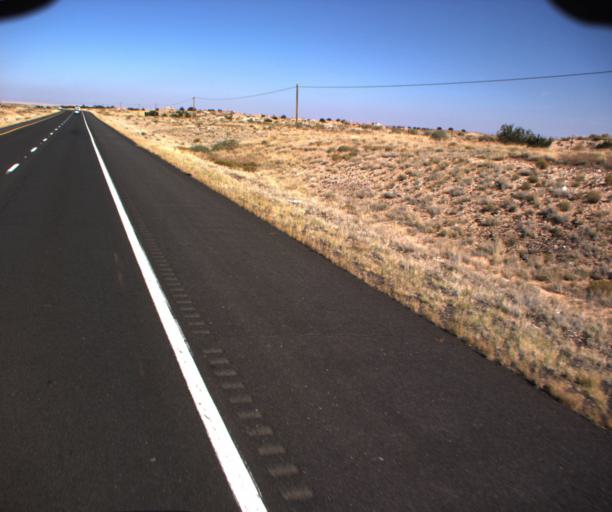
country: US
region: Arizona
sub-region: Coconino County
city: Flagstaff
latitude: 35.5122
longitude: -111.5457
